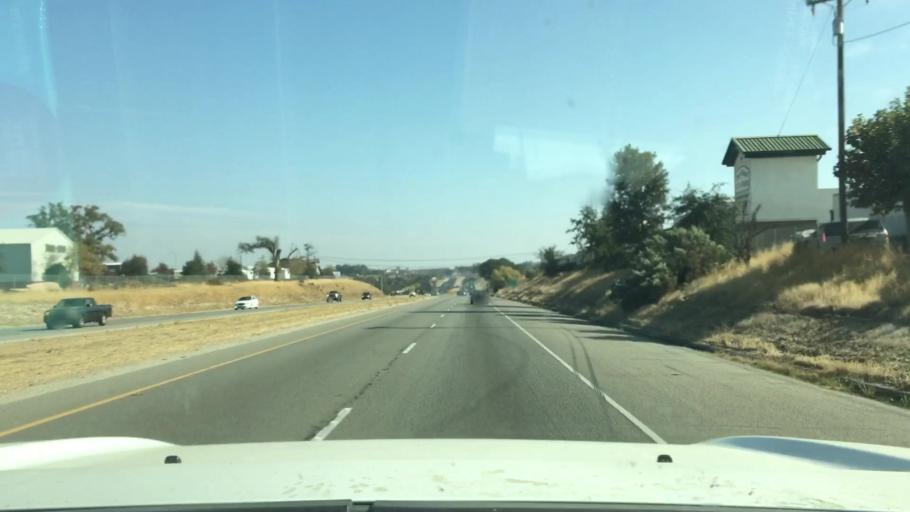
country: US
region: California
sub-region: San Luis Obispo County
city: Paso Robles
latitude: 35.6445
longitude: -120.6537
